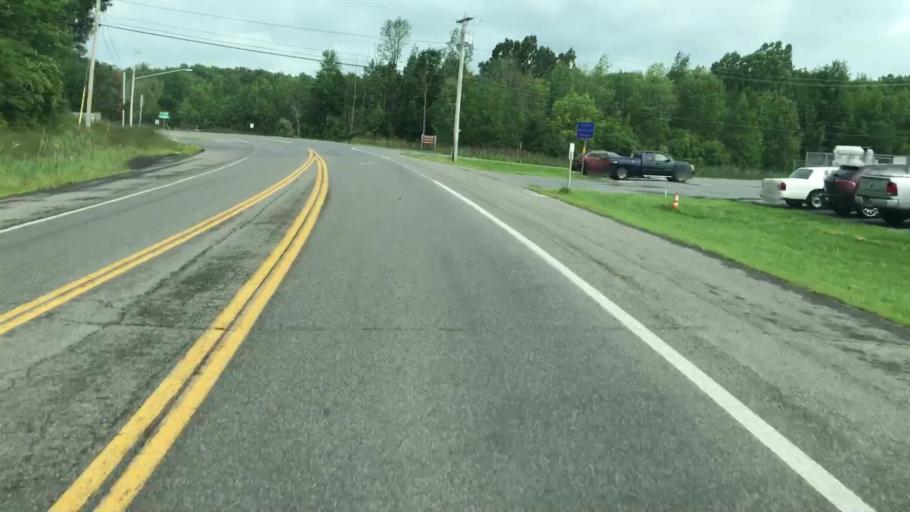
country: US
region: New York
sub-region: Onondaga County
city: Camillus
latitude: 43.0500
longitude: -76.3054
